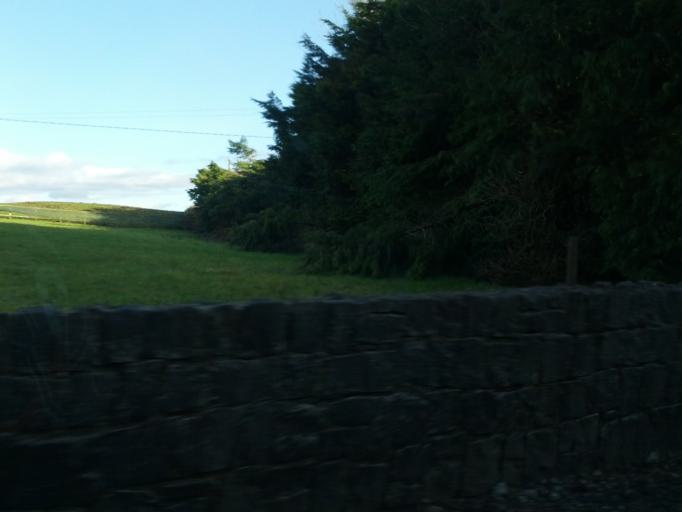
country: IE
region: Connaught
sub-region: County Galway
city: Athenry
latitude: 53.3856
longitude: -8.5834
